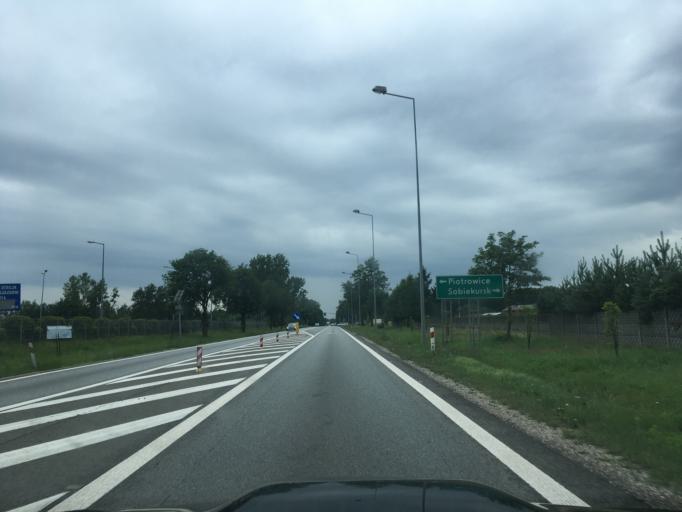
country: PL
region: Masovian Voivodeship
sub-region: Powiat otwocki
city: Karczew
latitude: 52.0176
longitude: 21.2912
